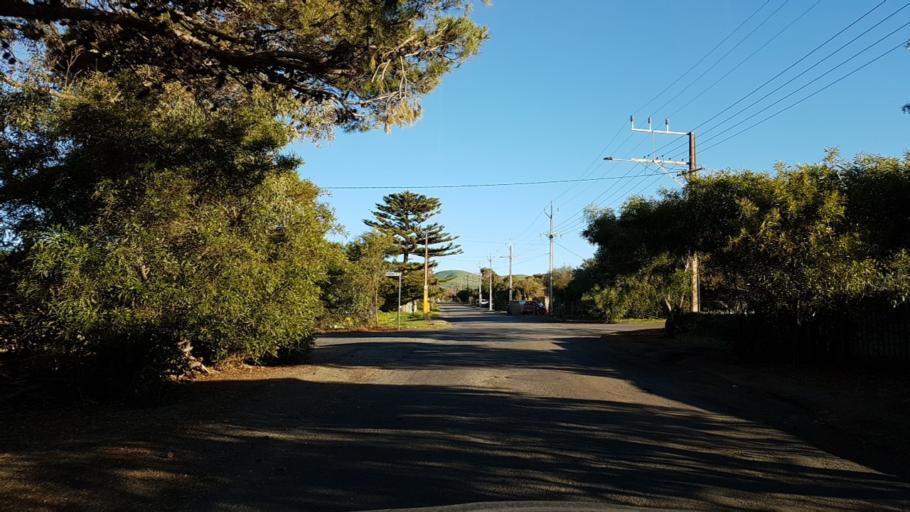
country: AU
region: South Australia
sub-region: Onkaparinga
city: Port Willunga
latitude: -35.3345
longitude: 138.4504
